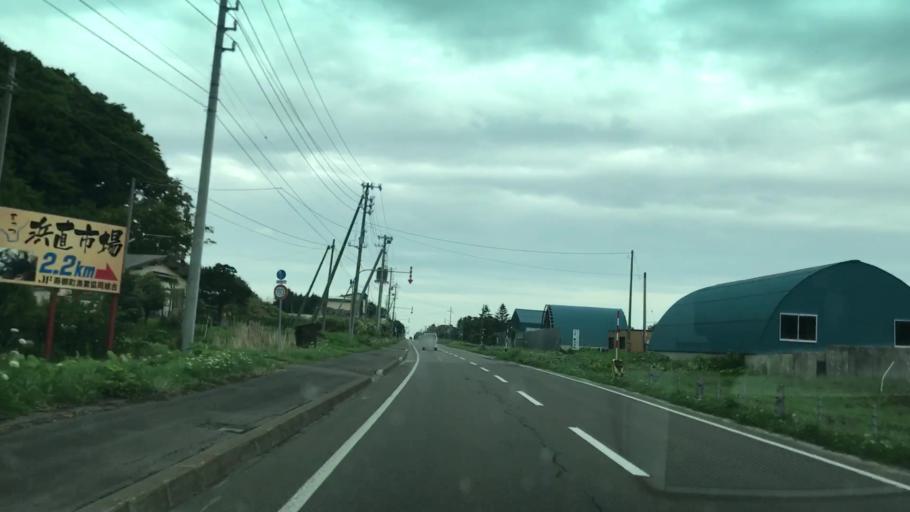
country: JP
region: Hokkaido
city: Iwanai
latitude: 42.7802
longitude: 140.2377
